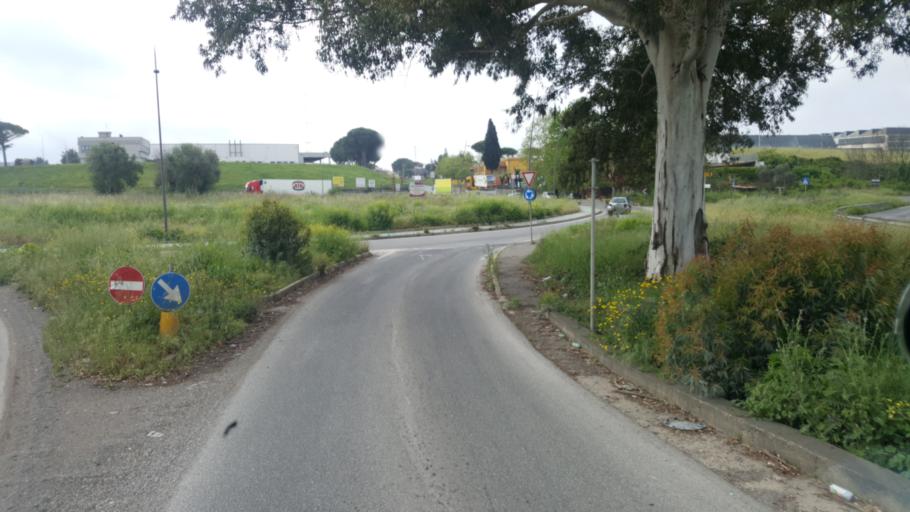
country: IT
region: Latium
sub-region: Citta metropolitana di Roma Capitale
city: Pavona
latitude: 41.7158
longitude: 12.5746
